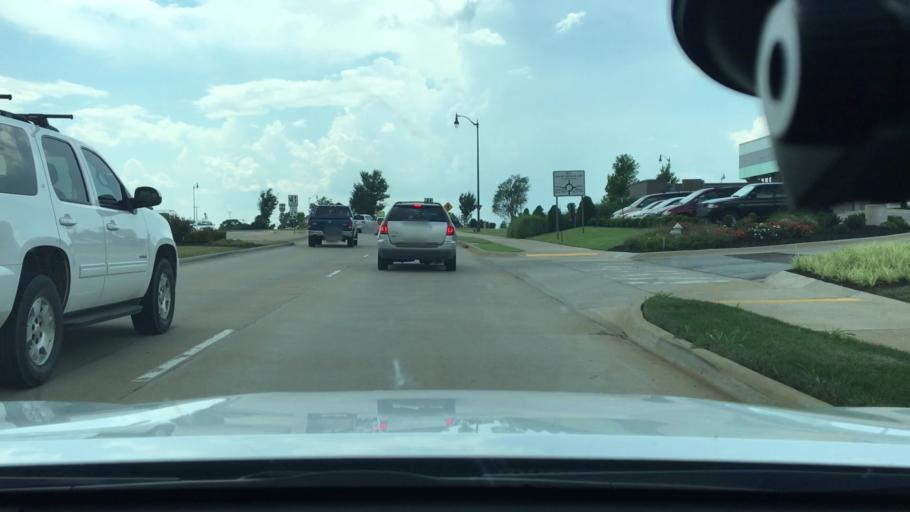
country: US
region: Arkansas
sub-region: Benton County
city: Cave Springs
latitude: 36.2976
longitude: -94.1853
